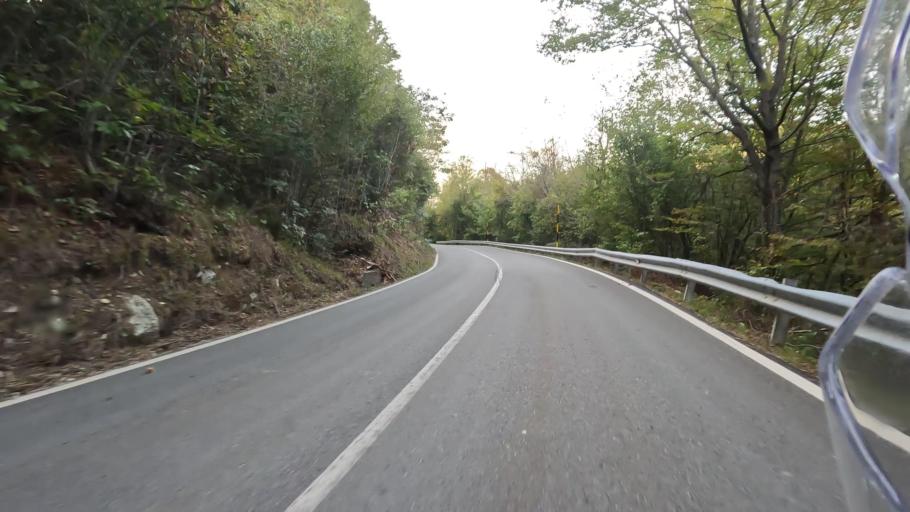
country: IT
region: Liguria
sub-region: Provincia di Savona
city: Sassello
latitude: 44.5084
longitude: 8.4817
